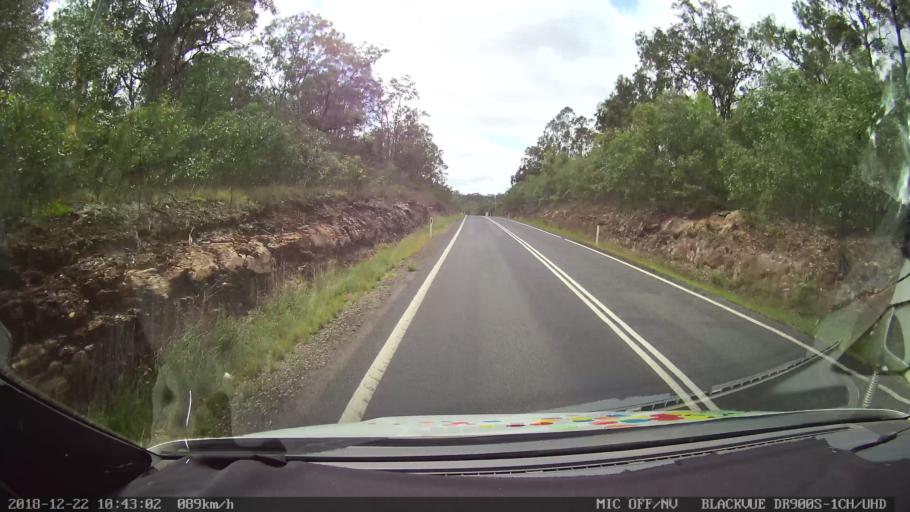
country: AU
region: New South Wales
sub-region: Clarence Valley
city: South Grafton
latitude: -29.6417
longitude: 152.7839
